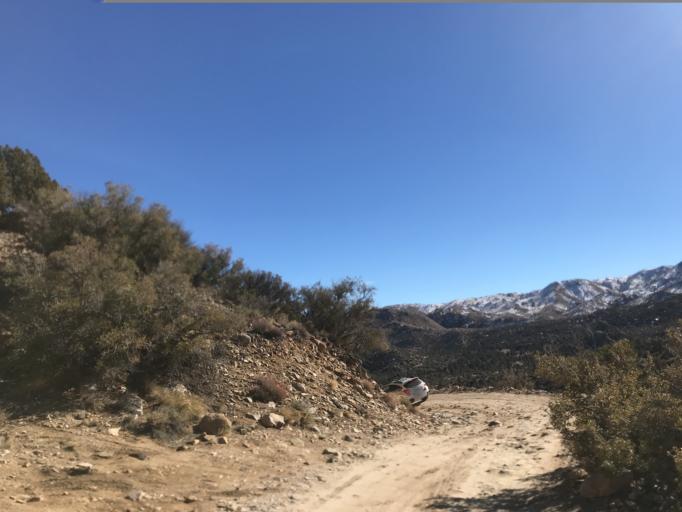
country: US
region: California
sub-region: San Bernardino County
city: Big Bear City
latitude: 34.2313
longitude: -116.6797
